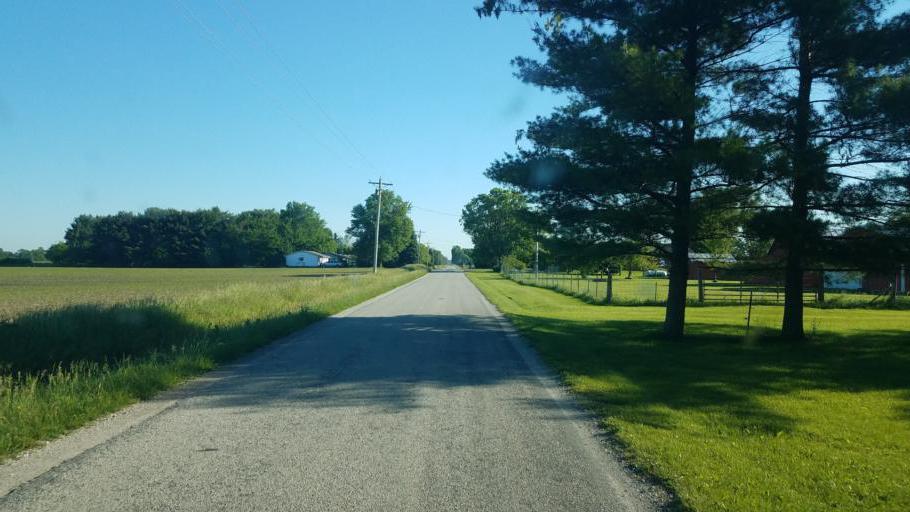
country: US
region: Ohio
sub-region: Marion County
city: Marion
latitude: 40.6219
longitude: -82.9909
